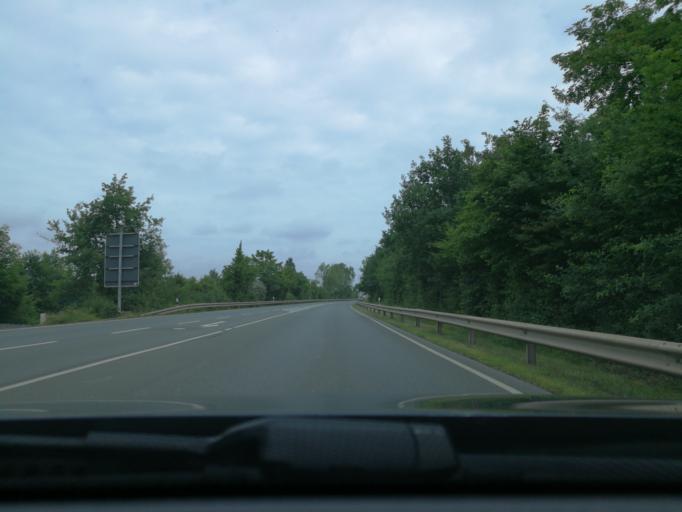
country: DE
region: Bavaria
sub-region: Regierungsbezirk Mittelfranken
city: Zirndorf
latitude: 49.4870
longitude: 10.9431
